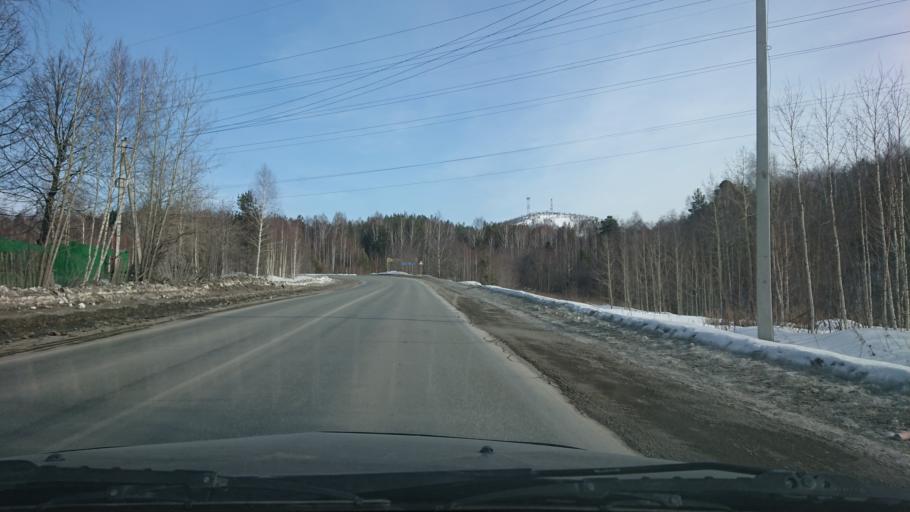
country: RU
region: Sverdlovsk
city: Revda
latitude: 56.8219
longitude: 59.9787
